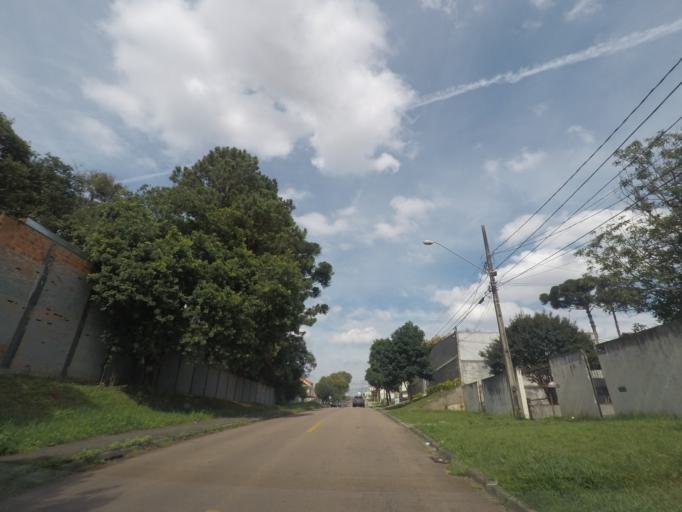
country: BR
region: Parana
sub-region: Sao Jose Dos Pinhais
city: Sao Jose dos Pinhais
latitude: -25.4916
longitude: -49.2591
